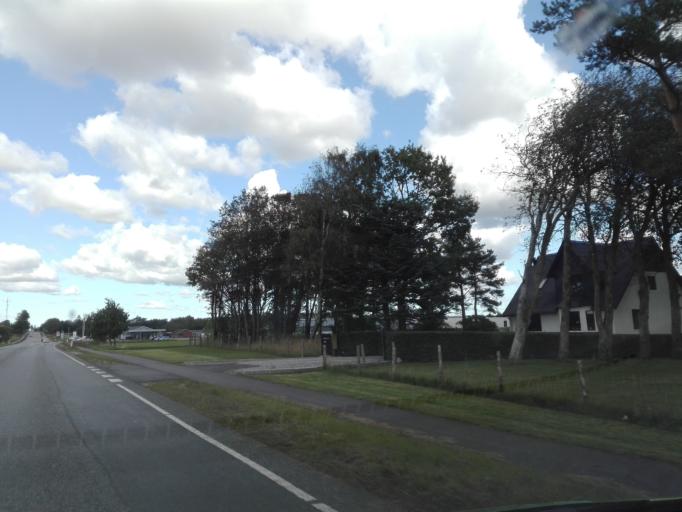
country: DK
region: North Denmark
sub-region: Mariagerfjord Kommune
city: Hobro
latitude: 56.6141
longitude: 9.8067
